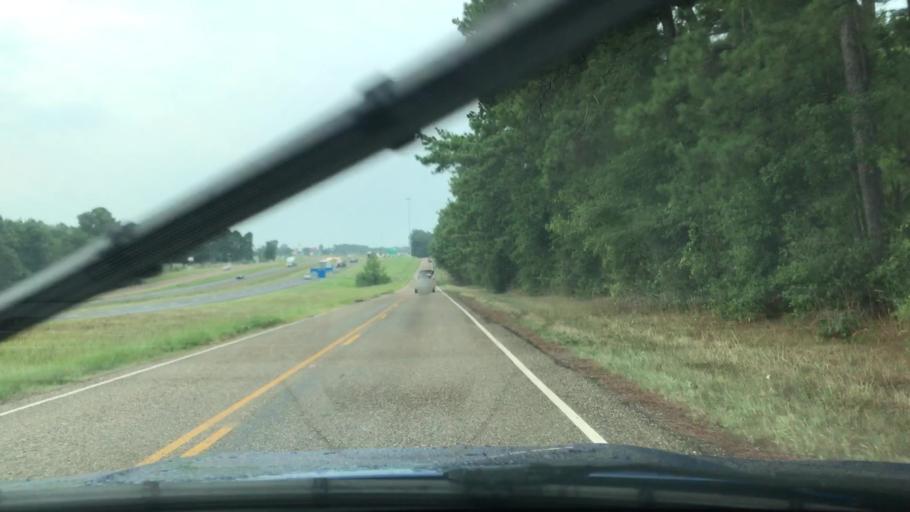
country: US
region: Texas
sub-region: Harrison County
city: Waskom
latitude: 32.4806
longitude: -94.0984
